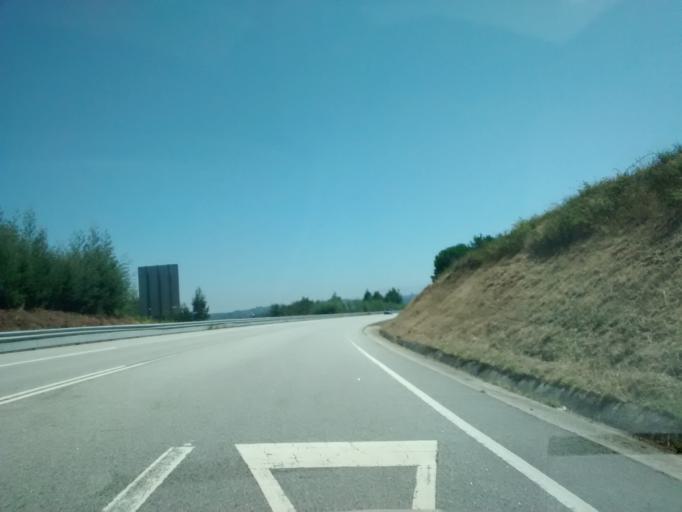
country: PT
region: Coimbra
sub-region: Tabua
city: Tabua
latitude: 40.3721
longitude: -8.0367
